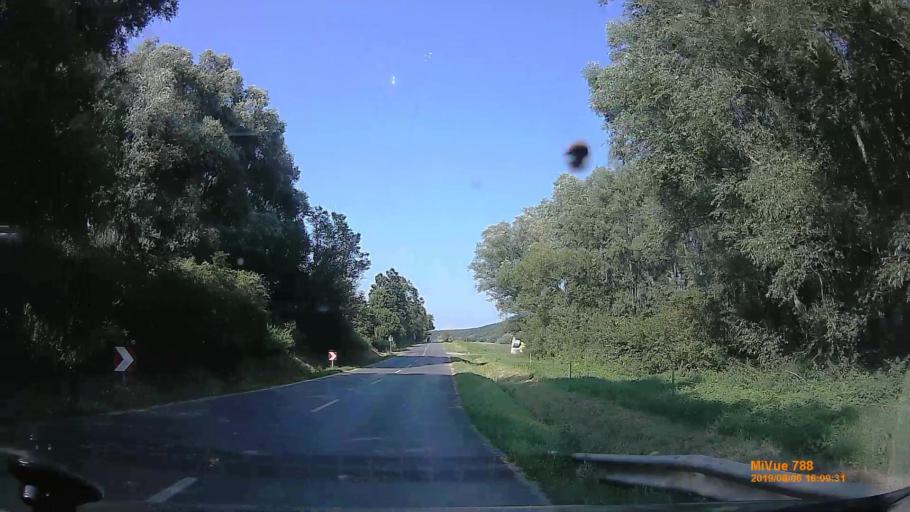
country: HU
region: Zala
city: Murakeresztur
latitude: 46.3368
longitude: 16.9720
